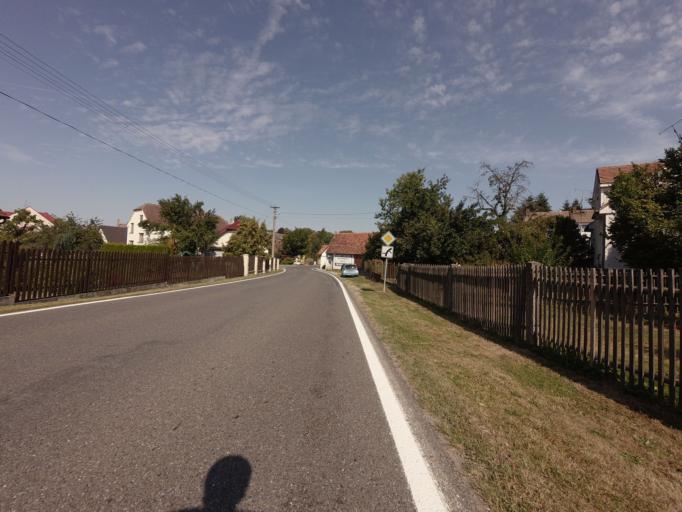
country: CZ
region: Jihocesky
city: Bernartice
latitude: 49.3876
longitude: 14.3586
